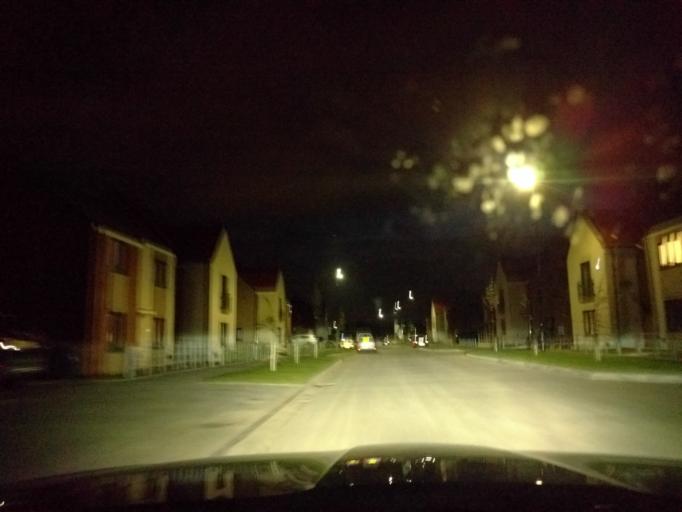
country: GB
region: England
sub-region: Borough of North Tyneside
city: Wallsend
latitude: 55.0112
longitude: -1.5457
